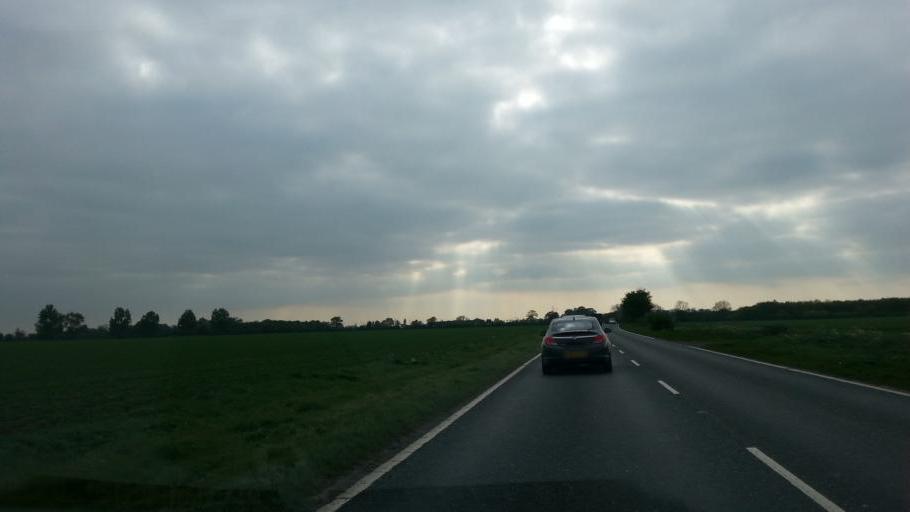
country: GB
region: England
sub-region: Lincolnshire
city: Navenby
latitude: 53.0691
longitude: -0.6453
